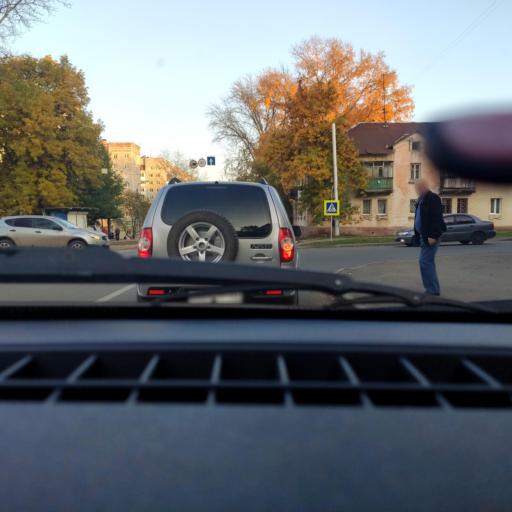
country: RU
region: Bashkortostan
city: Ufa
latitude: 54.8194
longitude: 56.1145
